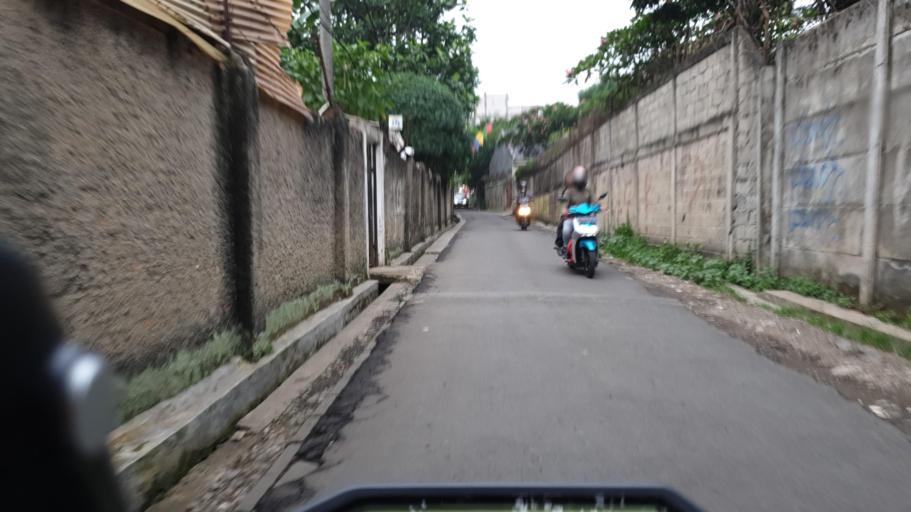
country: ID
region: West Java
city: Pamulang
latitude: -6.3257
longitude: 106.7706
